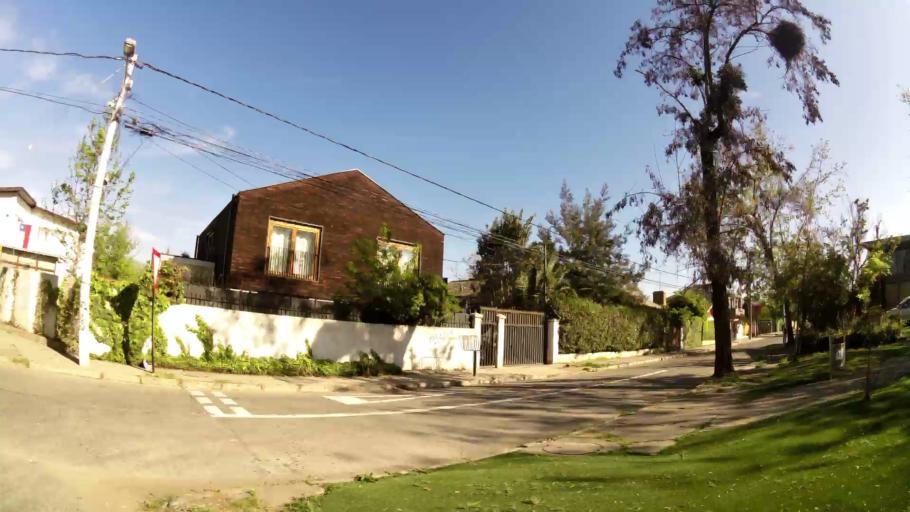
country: CL
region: Santiago Metropolitan
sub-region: Provincia de Santiago
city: Villa Presidente Frei, Nunoa, Santiago, Chile
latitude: -33.4360
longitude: -70.5556
